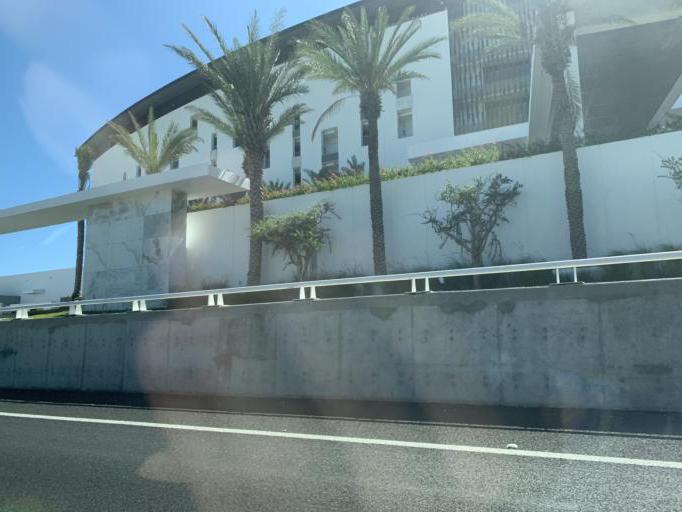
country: MX
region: Baja California Sur
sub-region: Los Cabos
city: San Jose del Cabo
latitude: 22.9723
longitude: -109.7859
